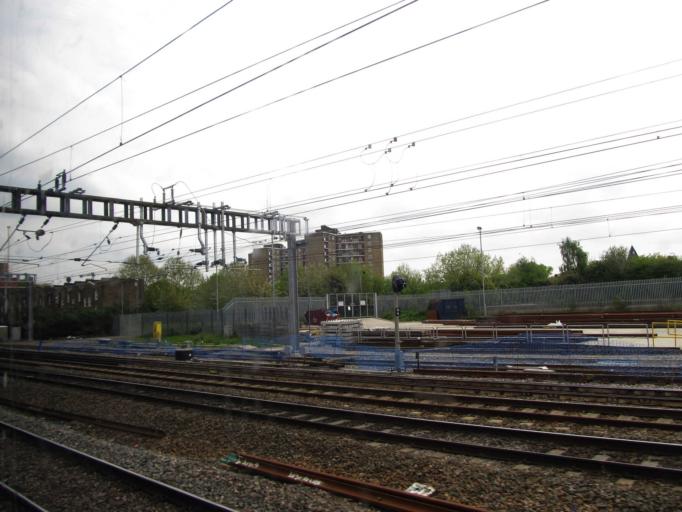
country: GB
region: England
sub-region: Greater London
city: Hammersmith
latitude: 51.5250
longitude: -0.2168
